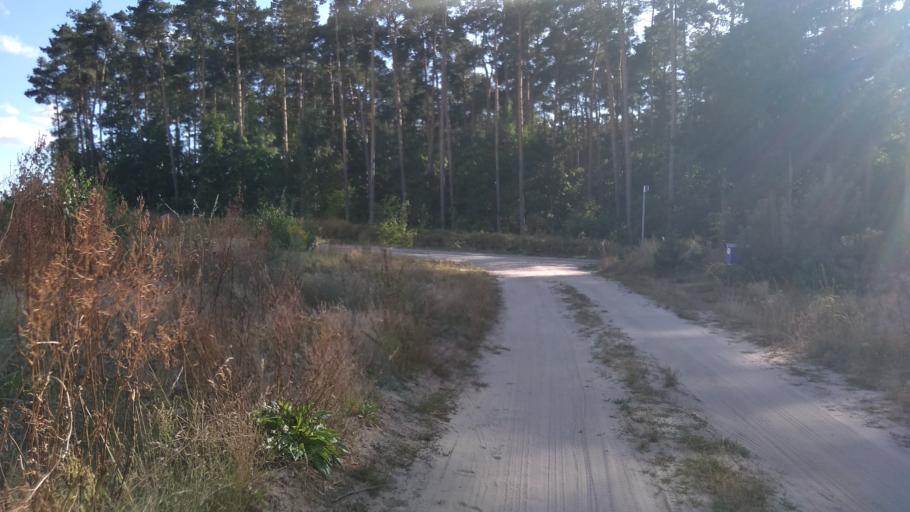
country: PL
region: Kujawsko-Pomorskie
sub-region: Powiat bydgoski
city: Osielsko
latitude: 53.2258
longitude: 18.1254
